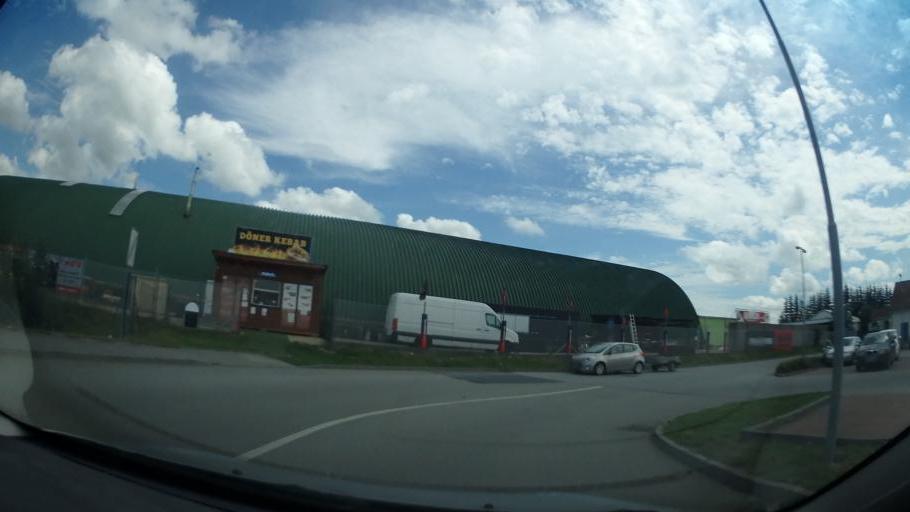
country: CZ
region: South Moravian
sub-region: Okres Brno-Venkov
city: Rosice
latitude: 49.1843
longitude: 16.4038
